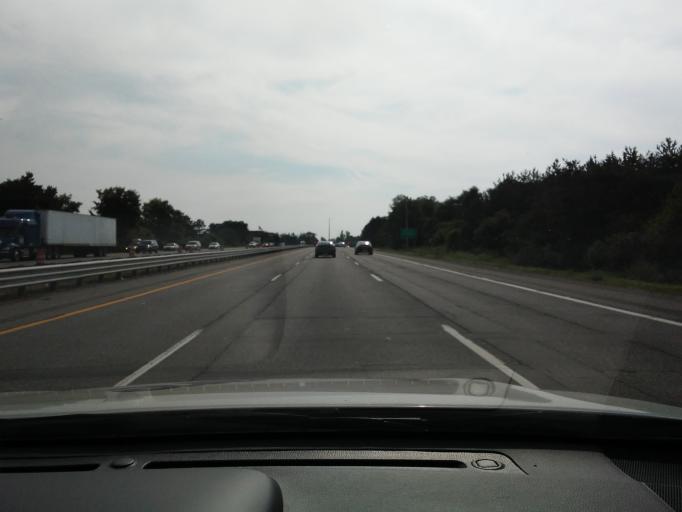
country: US
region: Michigan
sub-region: Oakland County
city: Troy
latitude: 42.6050
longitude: -83.1767
